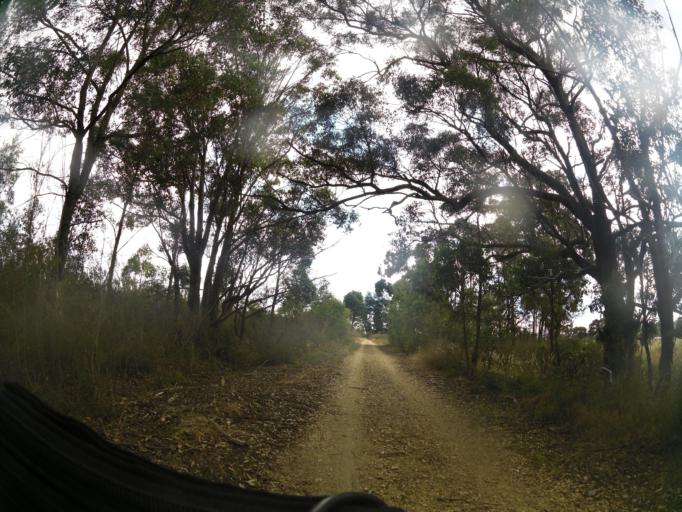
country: AU
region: Victoria
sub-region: Wellington
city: Heyfield
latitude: -38.0388
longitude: 146.6495
